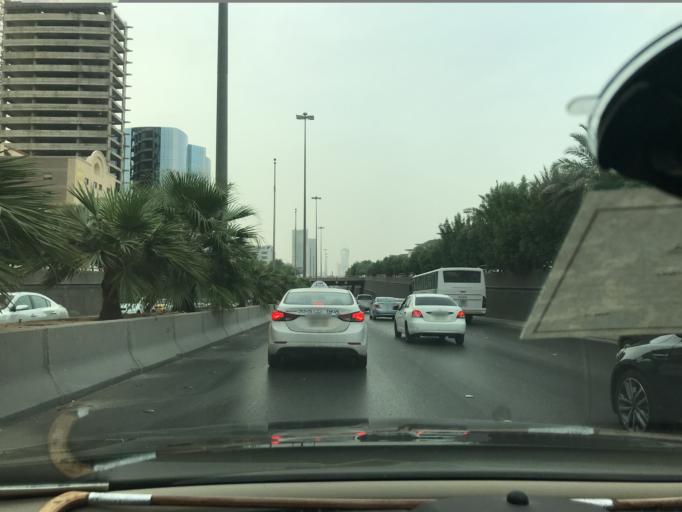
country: SA
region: Ar Riyad
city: Riyadh
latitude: 24.7097
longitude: 46.6730
